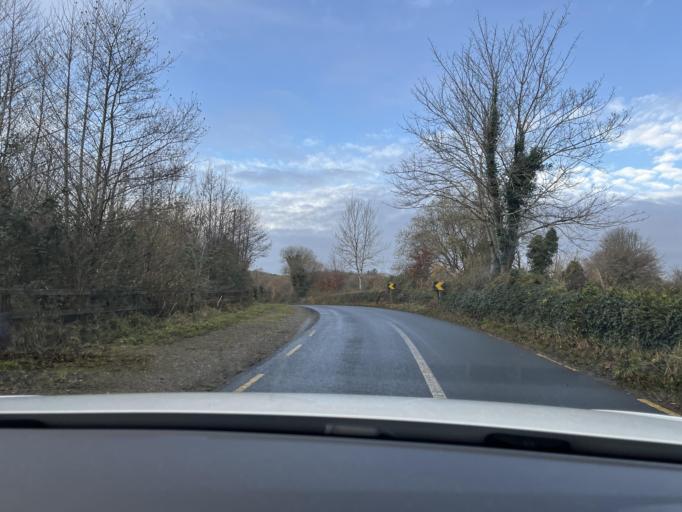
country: IE
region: Connaught
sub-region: Sligo
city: Sligo
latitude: 54.2645
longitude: -8.3626
